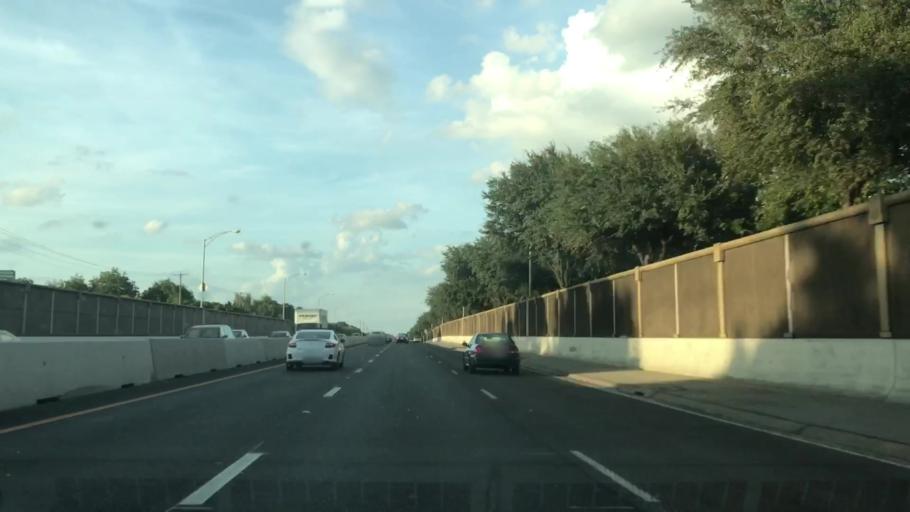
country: US
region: Texas
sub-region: Dallas County
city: University Park
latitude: 32.8534
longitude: -96.8129
